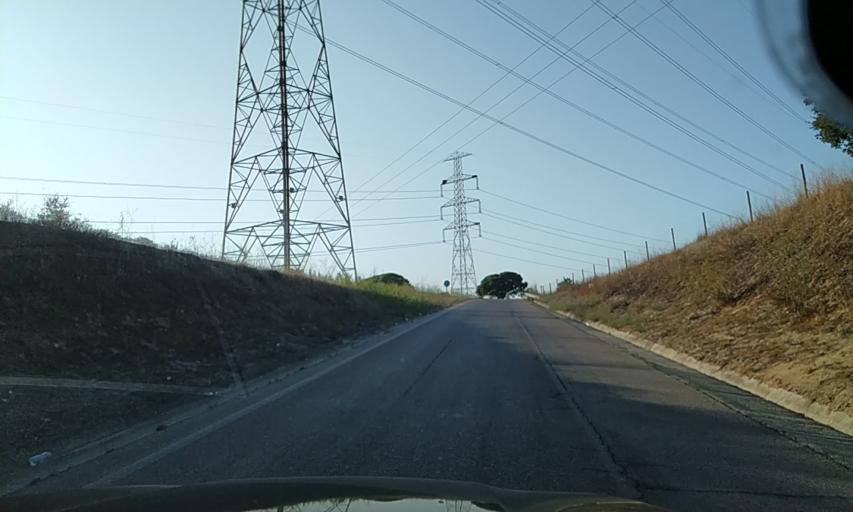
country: PT
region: Setubal
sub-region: Setubal
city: Setubal
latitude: 38.5246
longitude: -8.8431
